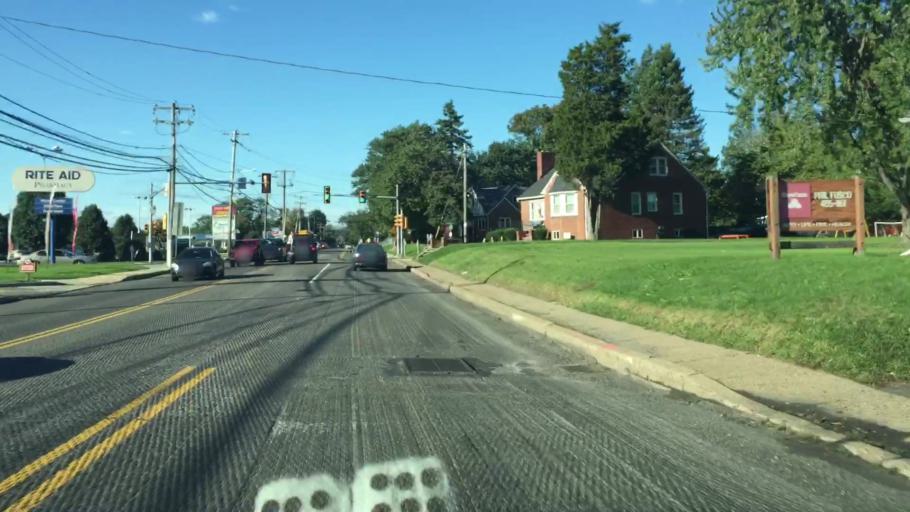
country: US
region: Pennsylvania
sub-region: Delaware County
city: Boothwyn
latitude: 39.8347
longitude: -75.4418
